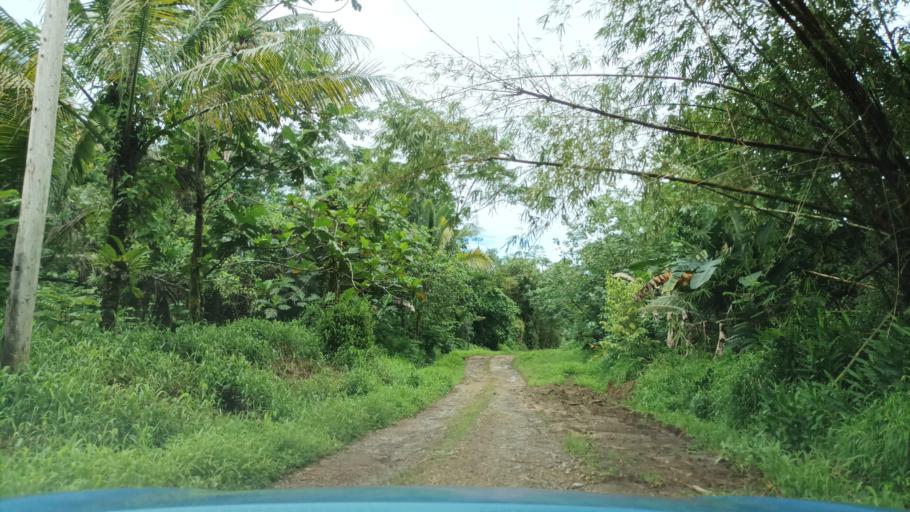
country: FM
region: Pohnpei
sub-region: Sokehs Municipality
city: Palikir - National Government Center
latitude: 6.8549
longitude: 158.1849
